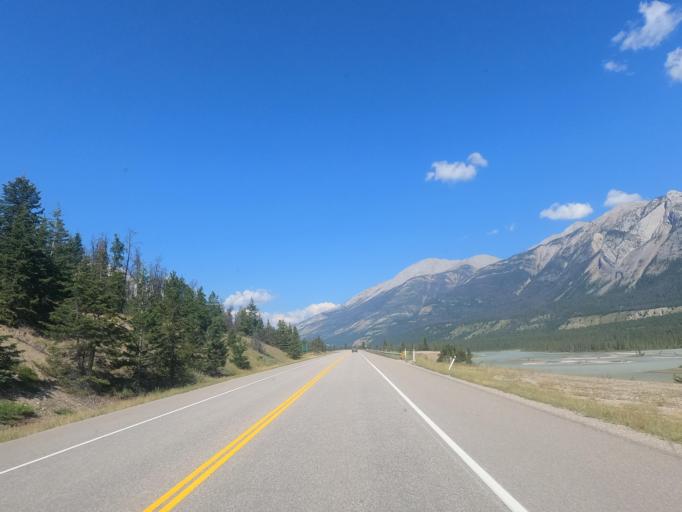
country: CA
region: Alberta
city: Jasper Park Lodge
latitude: 52.9439
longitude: -118.0394
